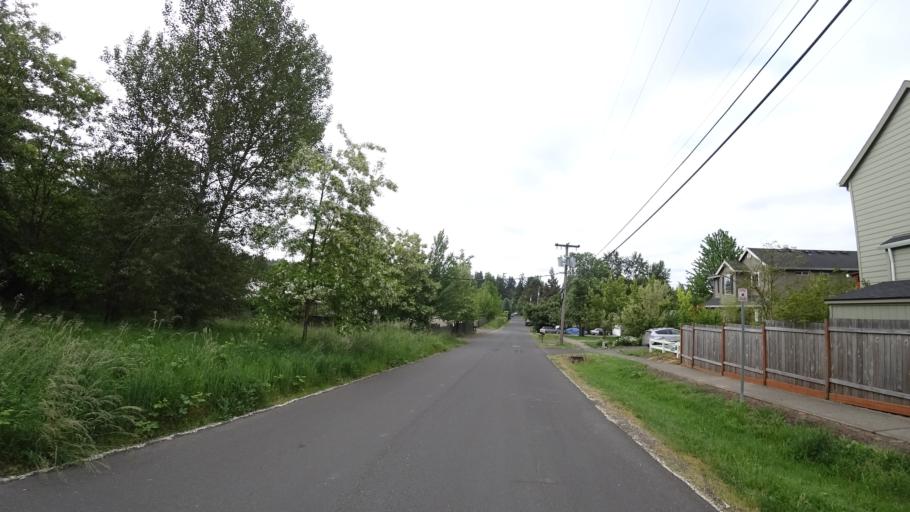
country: US
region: Oregon
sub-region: Washington County
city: Garden Home-Whitford
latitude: 45.4646
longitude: -122.7482
